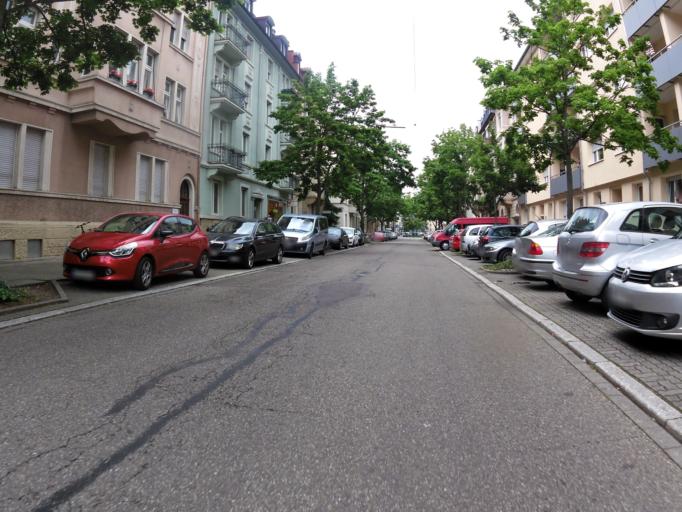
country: DE
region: Baden-Wuerttemberg
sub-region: Karlsruhe Region
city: Karlsruhe
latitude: 48.9985
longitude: 8.3925
